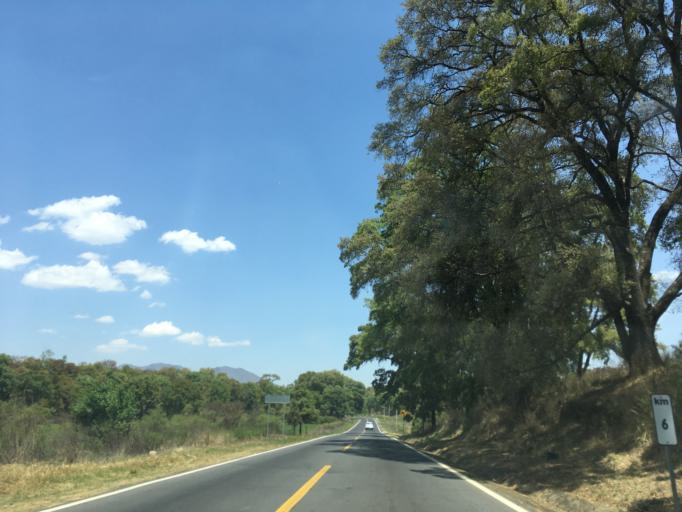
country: MX
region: Michoacan
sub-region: Chilchota
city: Tacuro (Santa Maria Tacuro)
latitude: 19.8013
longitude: -102.0249
